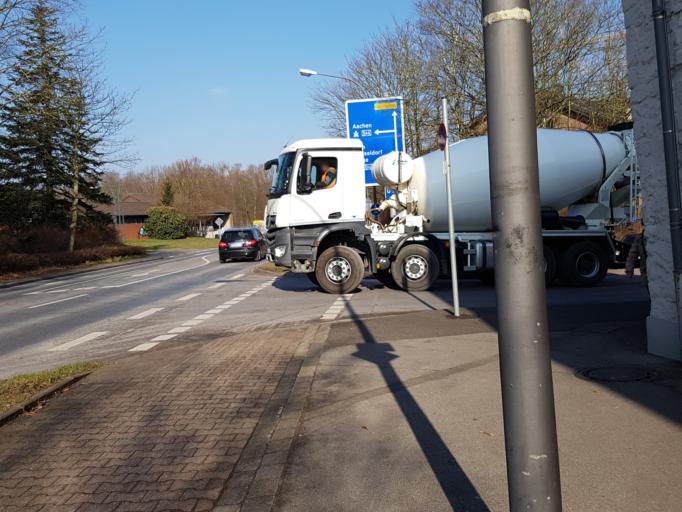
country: DE
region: North Rhine-Westphalia
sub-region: Regierungsbezirk Koln
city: Wurselen
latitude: 50.7985
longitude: 6.1532
